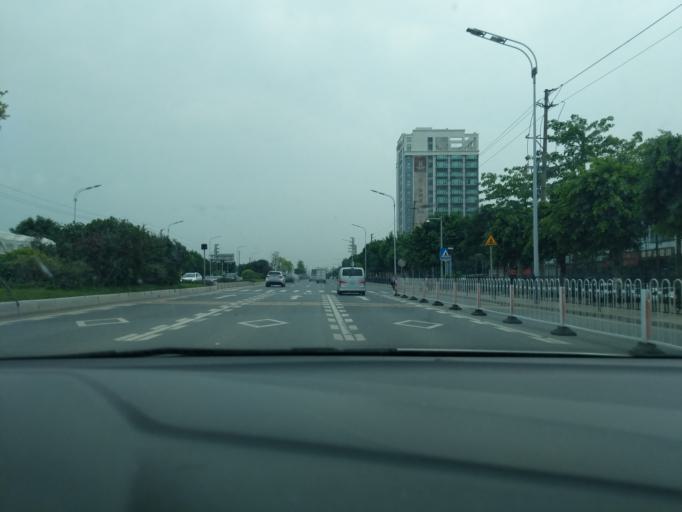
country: CN
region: Guangdong
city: Dongyong
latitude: 22.8650
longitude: 113.4813
